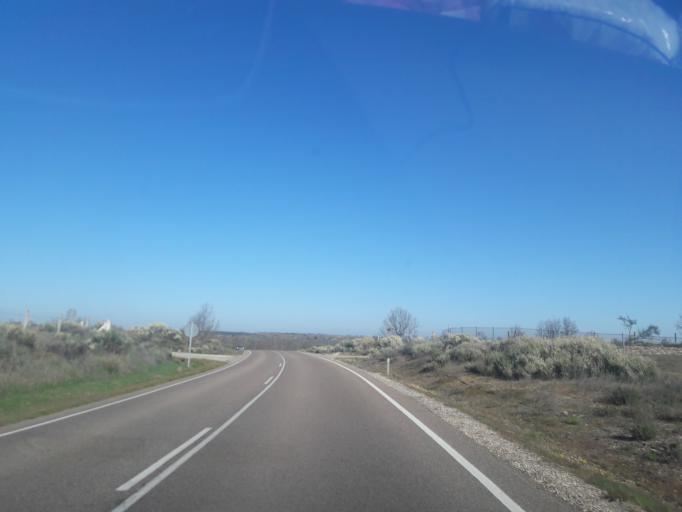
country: ES
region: Castille and Leon
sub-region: Provincia de Salamanca
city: Vitigudino
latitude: 41.0271
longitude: -6.4599
